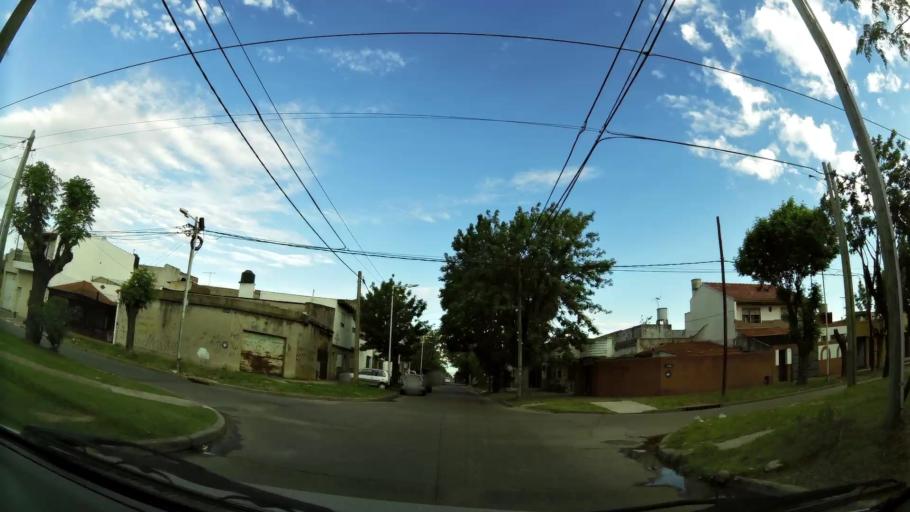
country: AR
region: Buenos Aires
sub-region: Partido de Avellaneda
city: Avellaneda
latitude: -34.6878
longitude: -58.3531
